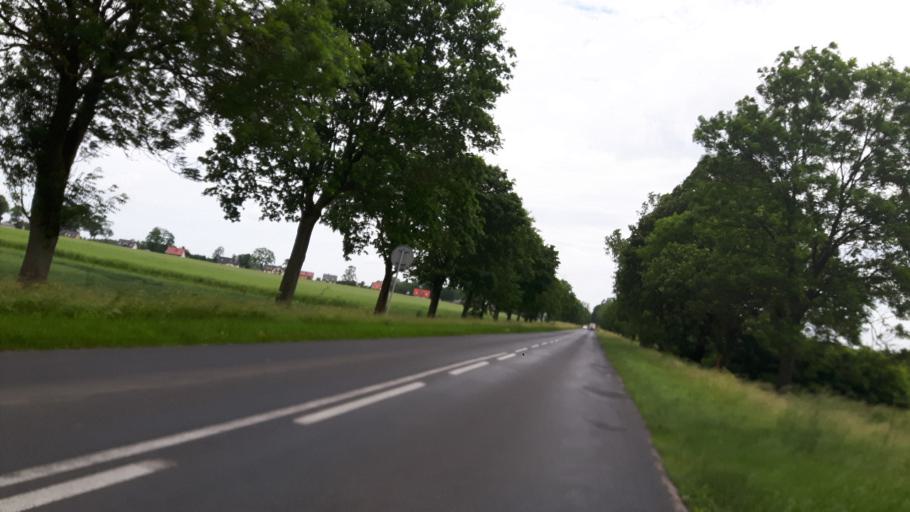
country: PL
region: West Pomeranian Voivodeship
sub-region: Powiat gryficki
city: Gryfice
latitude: 53.9373
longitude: 15.2168
